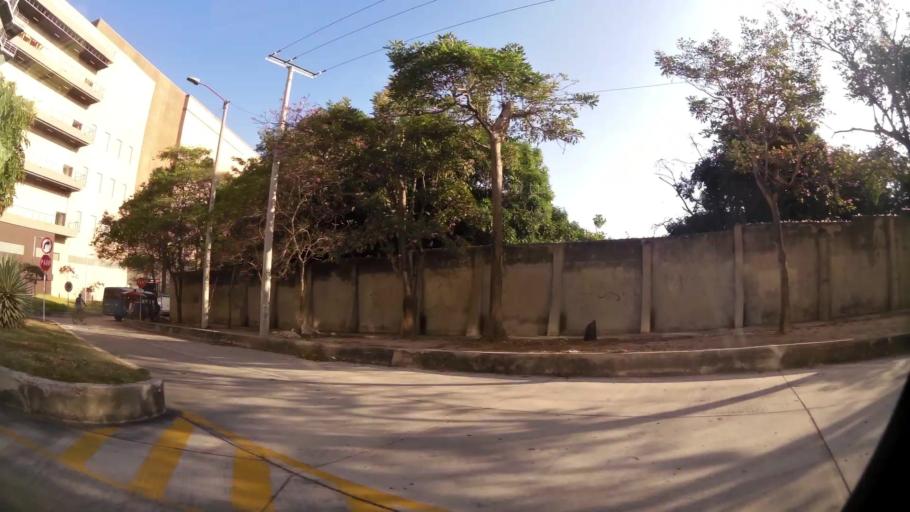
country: CO
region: Atlantico
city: Barranquilla
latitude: 11.0089
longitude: -74.8200
